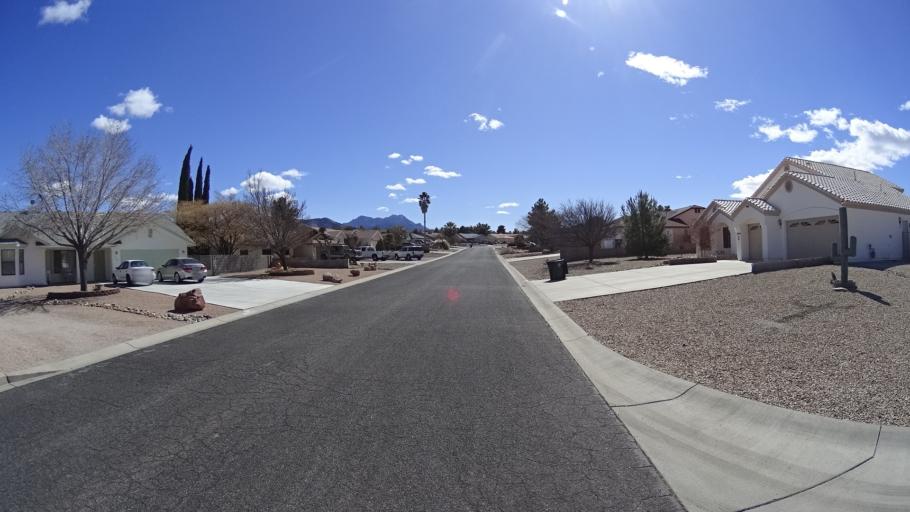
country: US
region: Arizona
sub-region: Mohave County
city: Kingman
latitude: 35.2025
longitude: -113.9708
